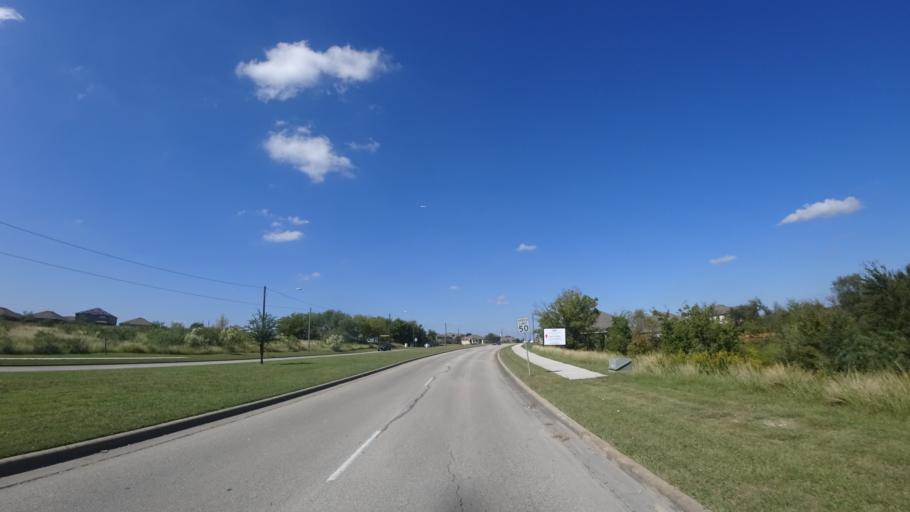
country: US
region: Texas
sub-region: Travis County
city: Manor
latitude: 30.3543
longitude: -97.6166
